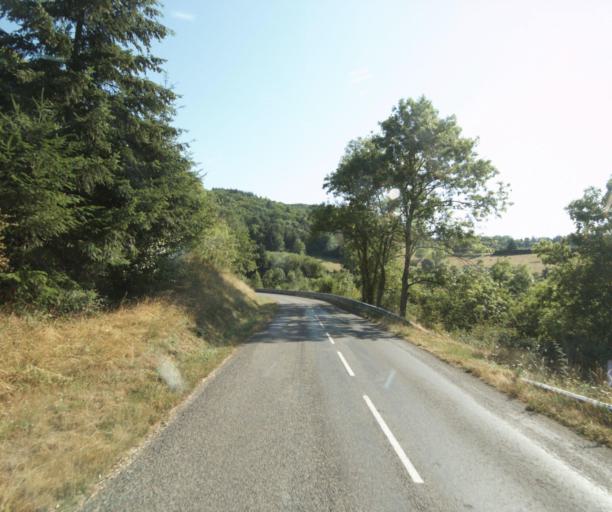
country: FR
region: Rhone-Alpes
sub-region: Departement du Rhone
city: Saint-Pierre-la-Palud
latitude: 45.7716
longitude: 4.6117
